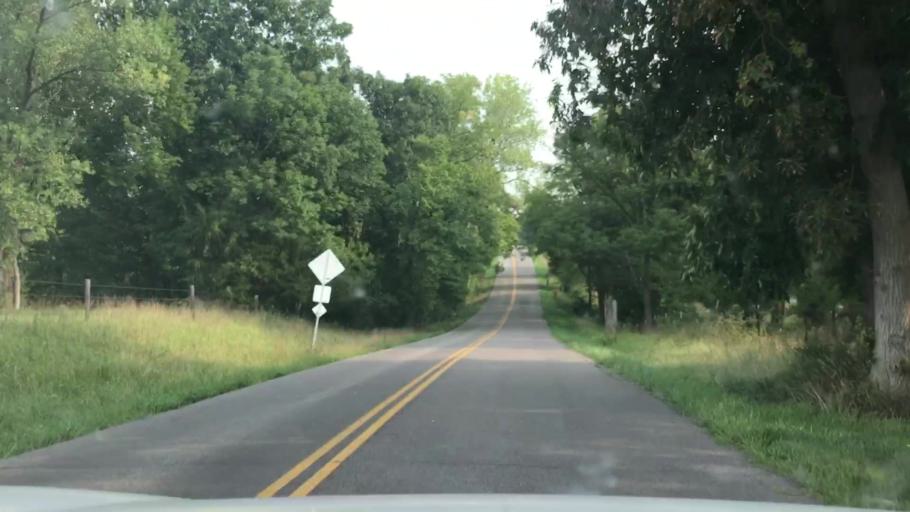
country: US
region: Missouri
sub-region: Saint Charles County
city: Cottleville
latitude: 38.7063
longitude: -90.6416
